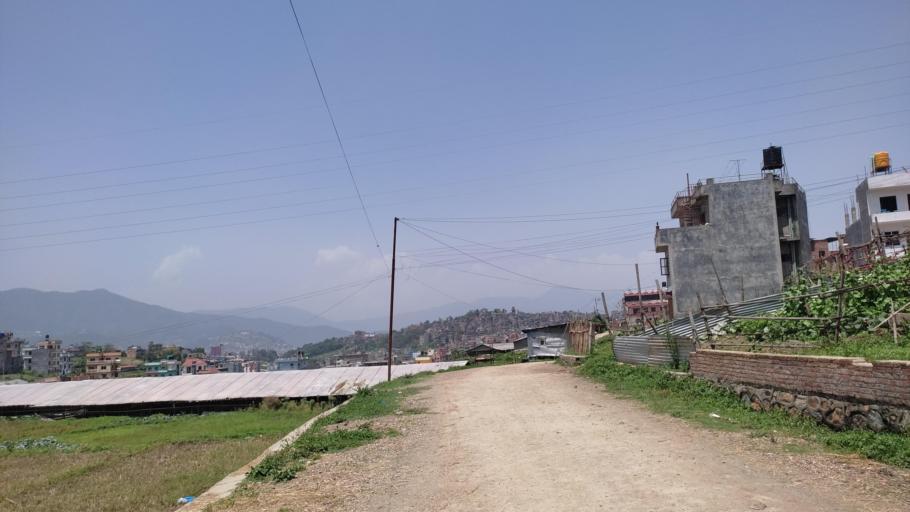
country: NP
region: Central Region
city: Kirtipur
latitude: 27.6687
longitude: 85.2666
